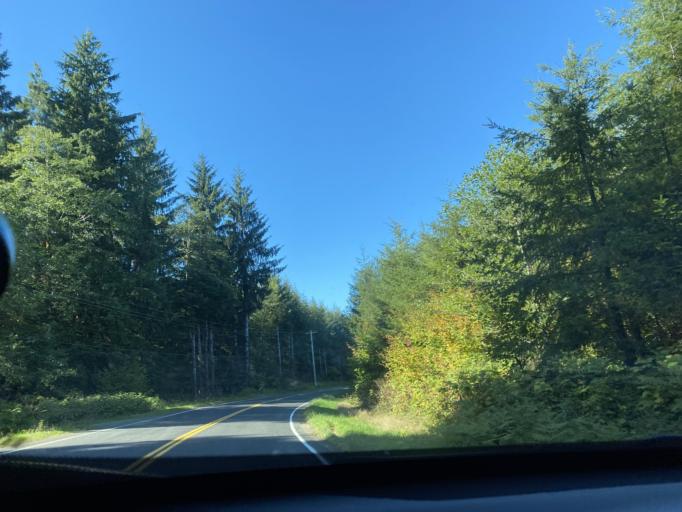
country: US
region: Washington
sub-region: Clallam County
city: Forks
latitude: 47.9510
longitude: -124.4706
